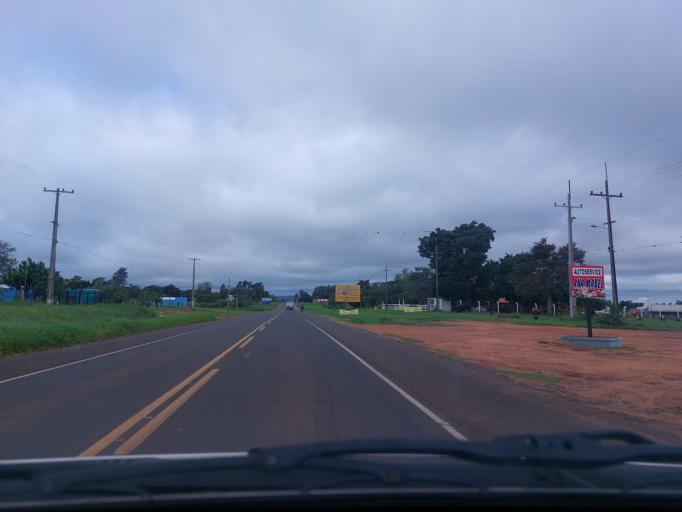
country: PY
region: San Pedro
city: Guayaybi
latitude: -24.6120
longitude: -56.3818
